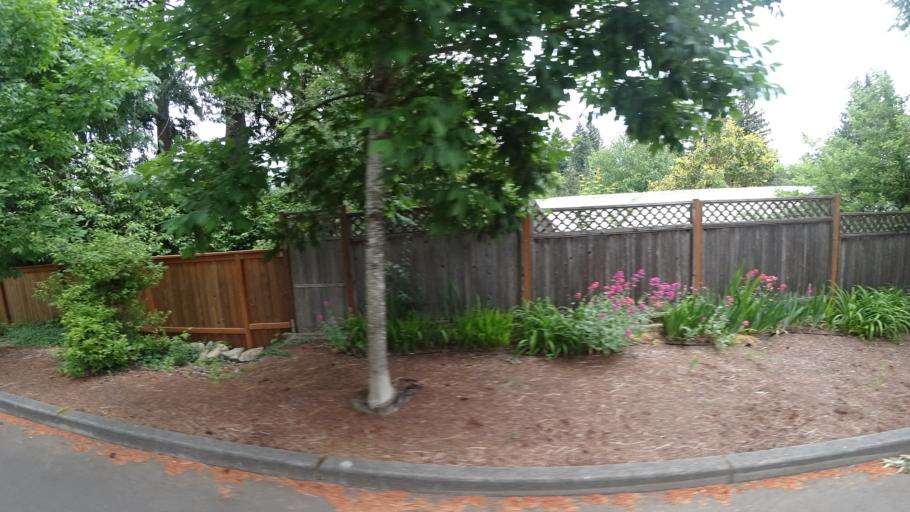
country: US
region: Oregon
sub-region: Clackamas County
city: Lake Oswego
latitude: 45.4575
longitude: -122.6919
